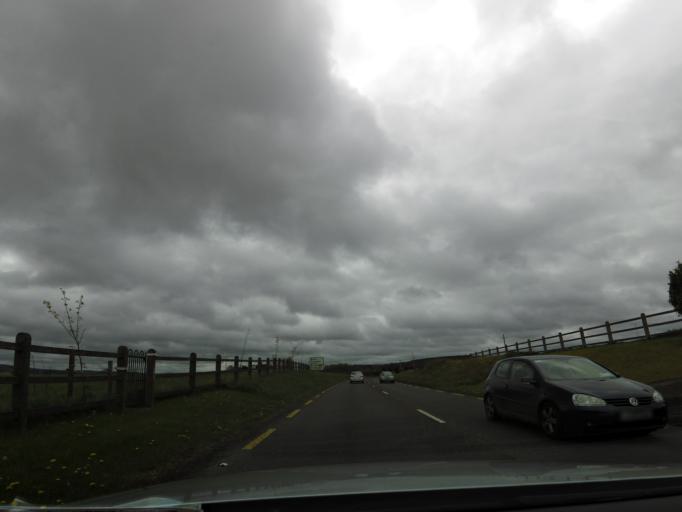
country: IE
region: Leinster
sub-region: Kilkenny
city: Ballyragget
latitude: 52.7156
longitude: -7.3316
